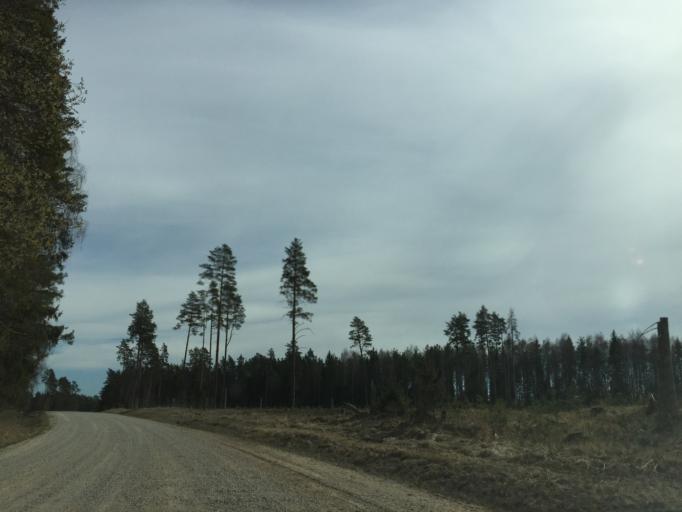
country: LV
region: Valkas Rajons
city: Valka
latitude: 57.8019
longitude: 25.9507
